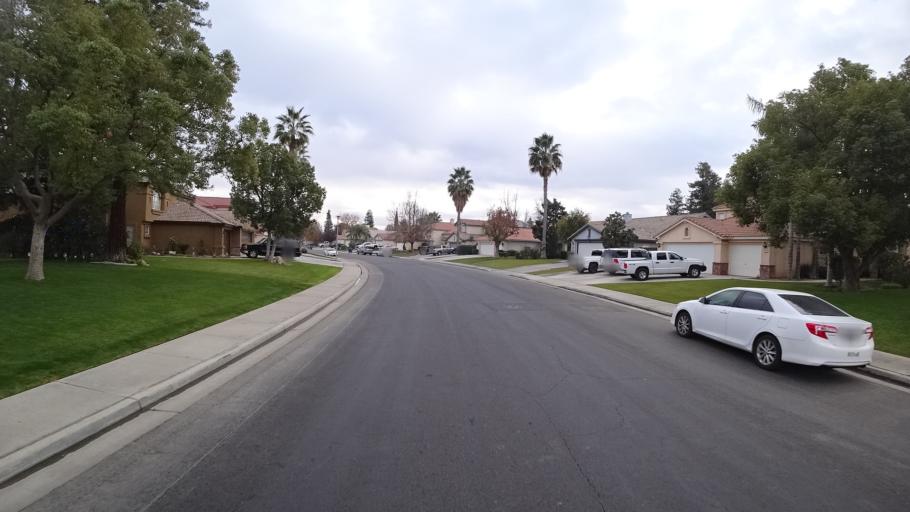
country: US
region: California
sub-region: Kern County
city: Greenacres
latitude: 35.3021
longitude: -119.0840
